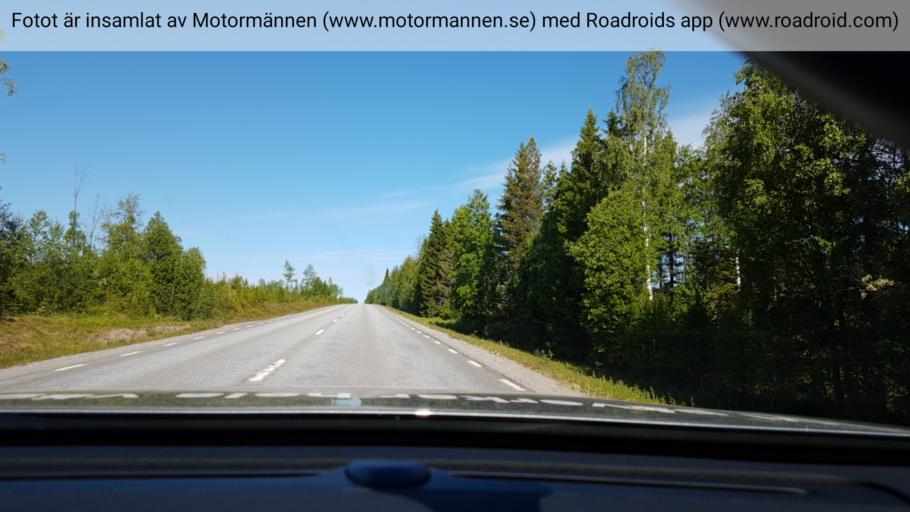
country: SE
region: Vaesterbotten
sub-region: Bjurholms Kommun
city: Bjurholm
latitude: 63.9456
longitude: 18.9119
